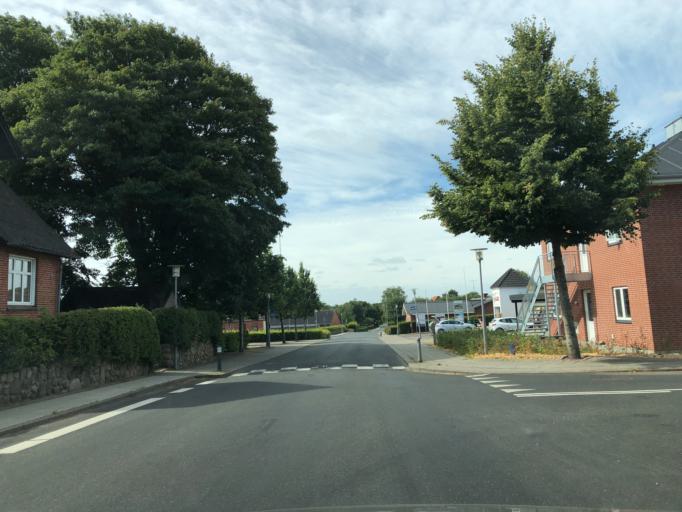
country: DK
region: Central Jutland
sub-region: Viborg Kommune
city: Viborg
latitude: 56.5350
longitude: 9.4684
